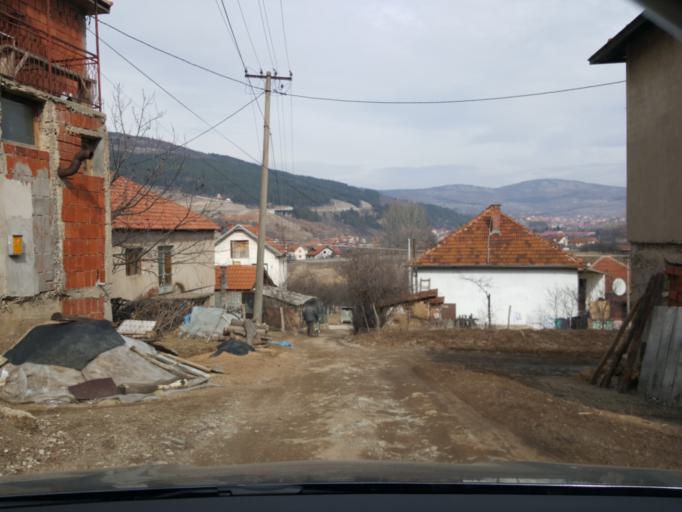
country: RS
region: Central Serbia
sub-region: Pirotski Okrug
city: Dimitrovgrad
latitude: 43.0080
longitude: 22.7529
